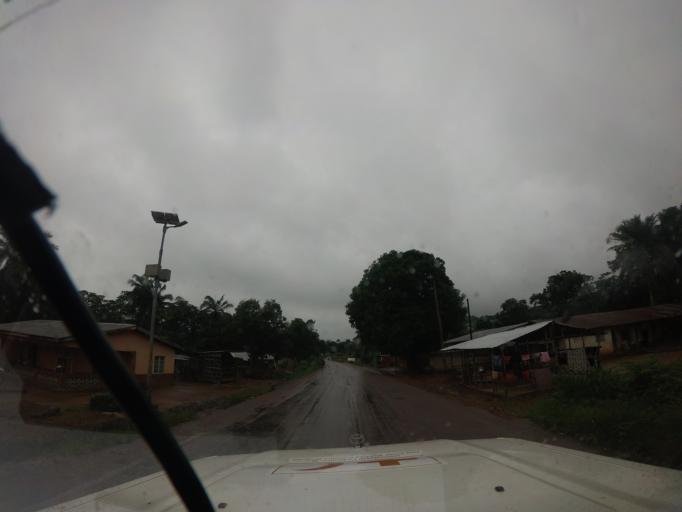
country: SL
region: Northern Province
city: Kabala
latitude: 9.5790
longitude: -11.5558
